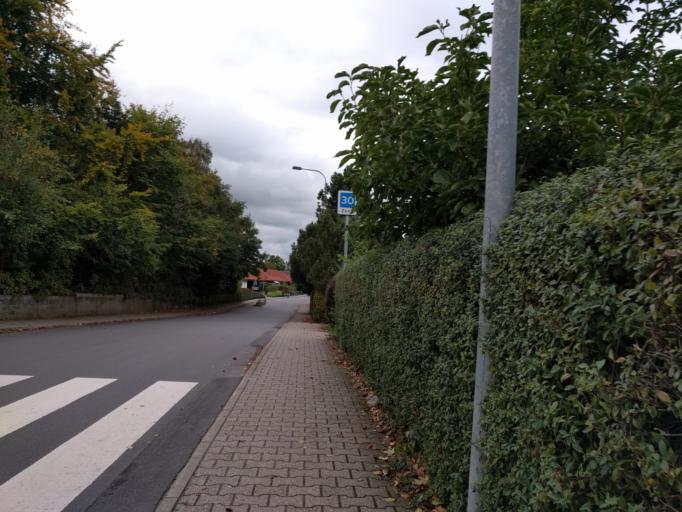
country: DK
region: South Denmark
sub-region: Fredericia Kommune
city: Snoghoj
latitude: 55.5448
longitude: 9.7130
